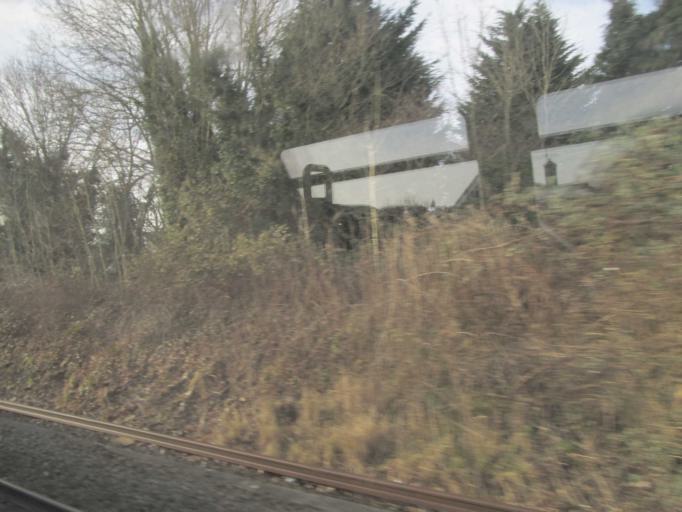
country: GB
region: England
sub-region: Wokingham
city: Wokingham
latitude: 51.4177
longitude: -0.8490
